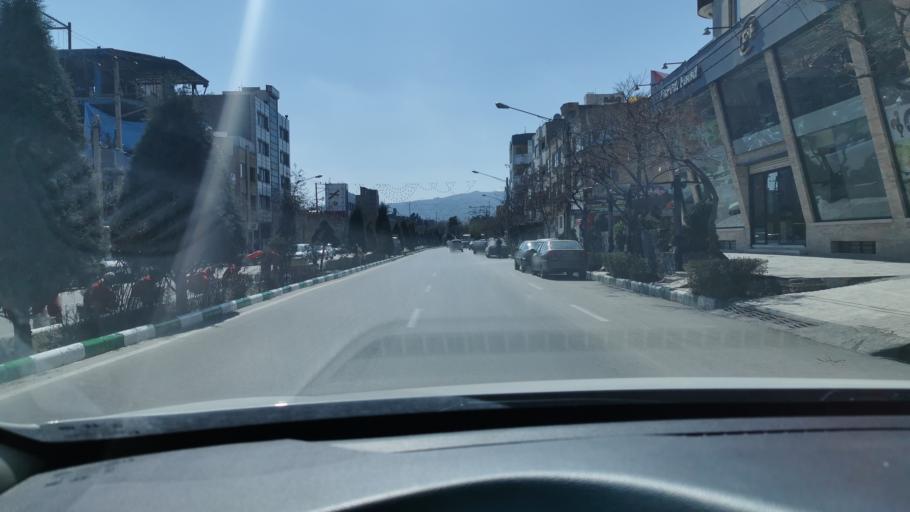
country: IR
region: Razavi Khorasan
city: Mashhad
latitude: 36.3226
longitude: 59.5257
